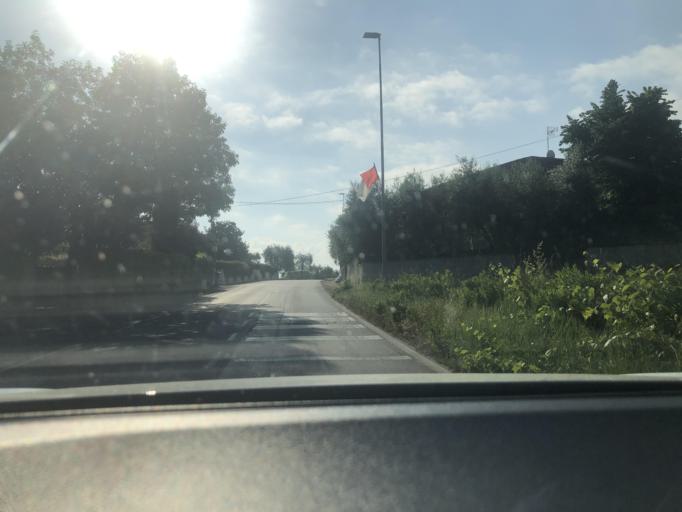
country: IT
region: Tuscany
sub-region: Provincia di Pistoia
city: Lamporecchio
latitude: 43.8064
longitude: 10.8689
